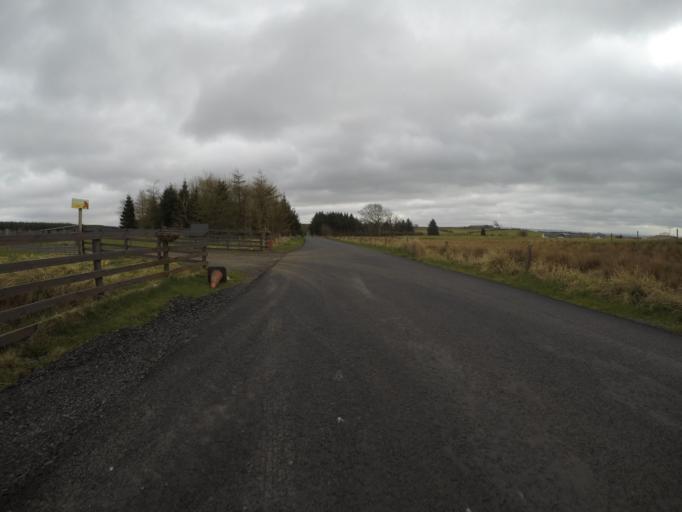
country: GB
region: Scotland
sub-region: East Ayrshire
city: Stewarton
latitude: 55.6808
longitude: -4.4559
